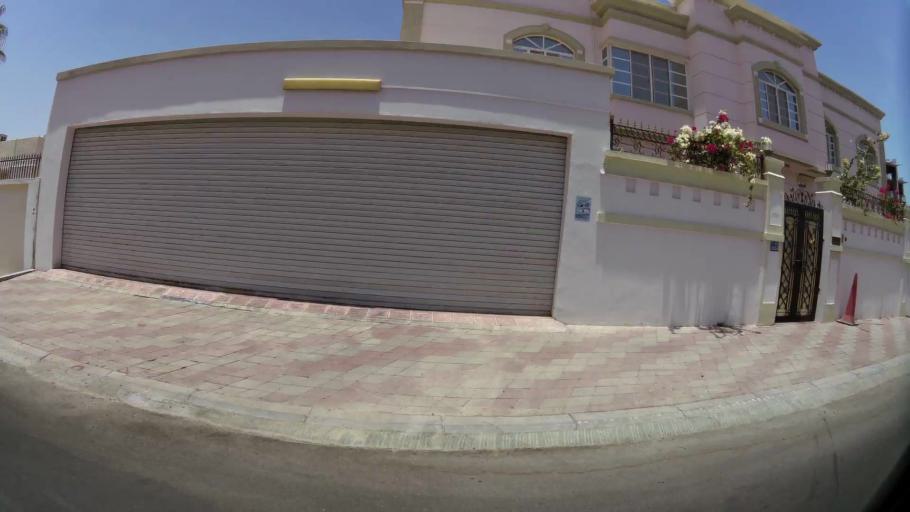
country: OM
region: Muhafazat Masqat
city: Bawshar
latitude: 23.6026
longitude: 58.4548
